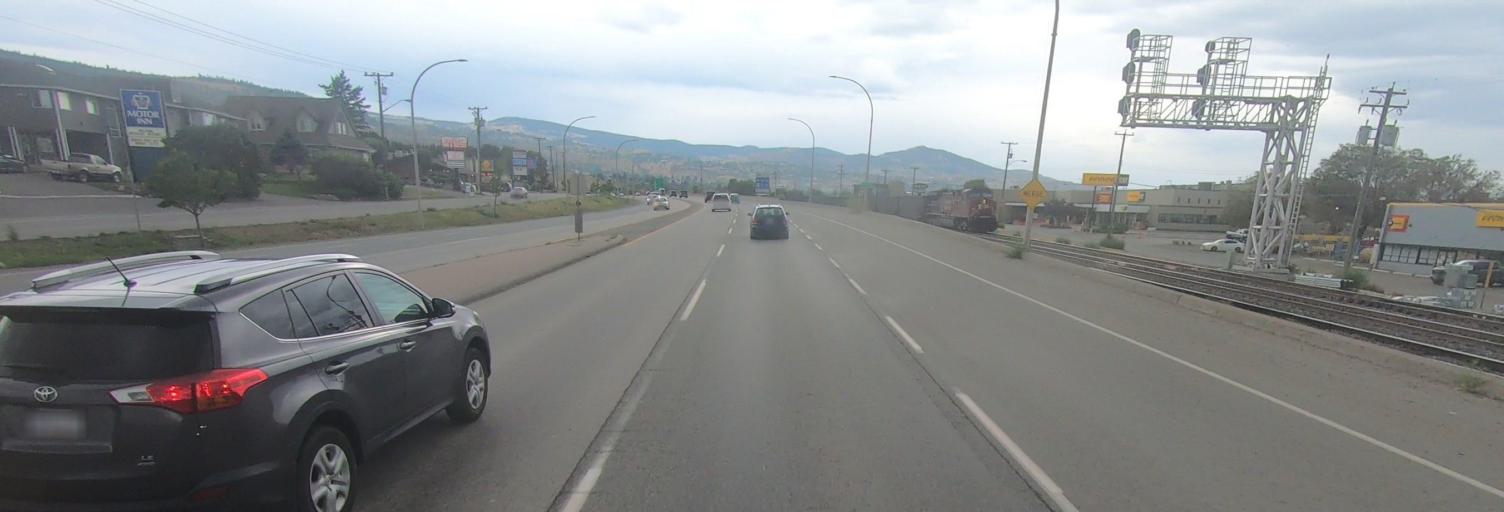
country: CA
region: British Columbia
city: Kamloops
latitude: 50.6783
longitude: -120.2851
